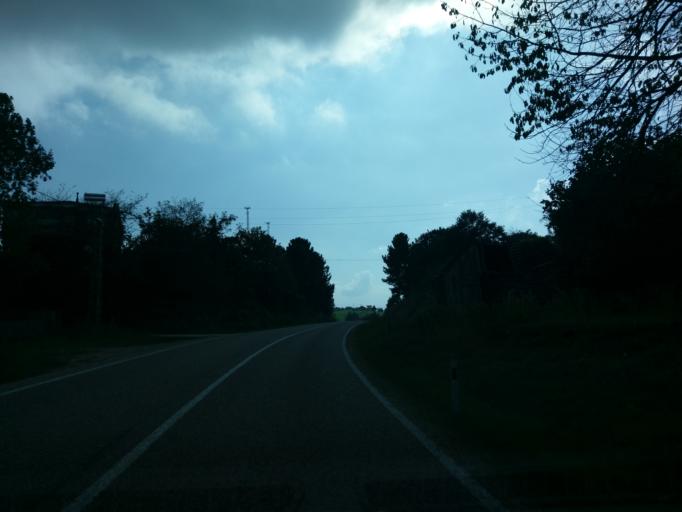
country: TR
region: Sinop
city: Erfelek
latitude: 41.9827
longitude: 34.8776
